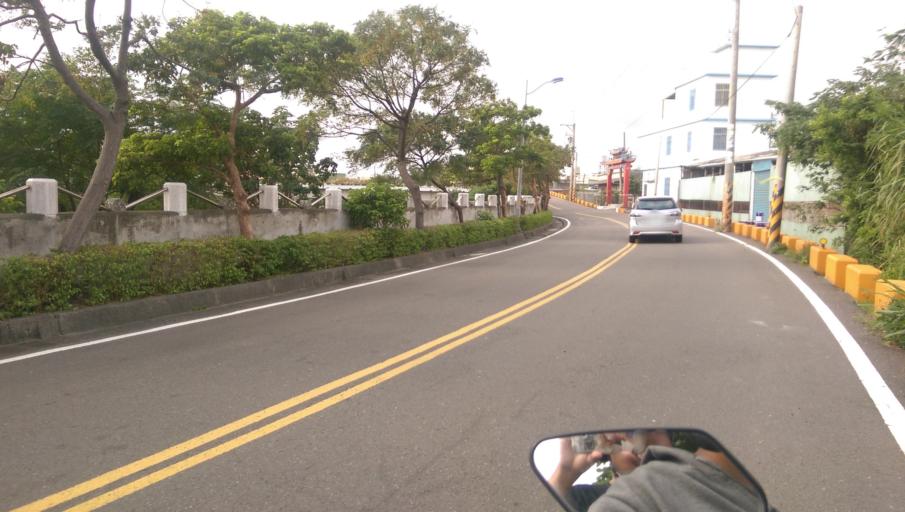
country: TW
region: Taiwan
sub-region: Hsinchu
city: Hsinchu
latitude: 24.8040
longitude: 120.9365
